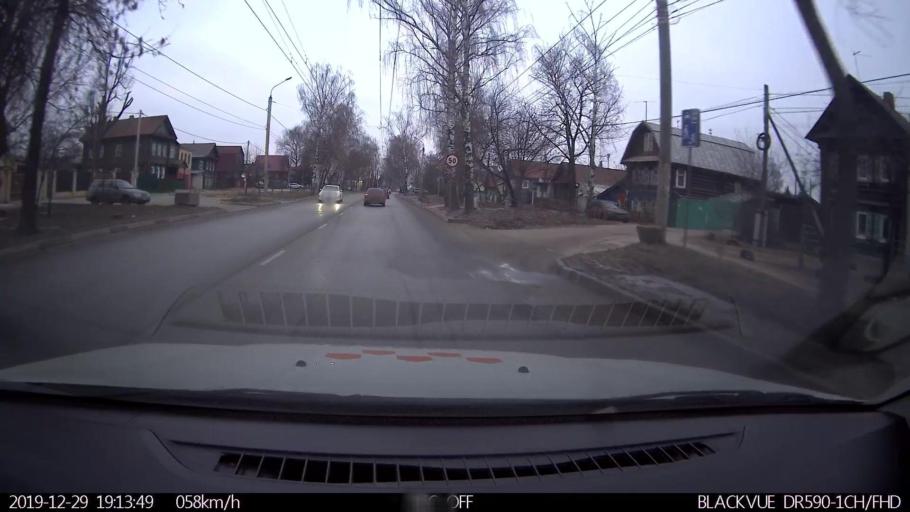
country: RU
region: Nizjnij Novgorod
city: Neklyudovo
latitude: 56.3643
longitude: 43.8521
